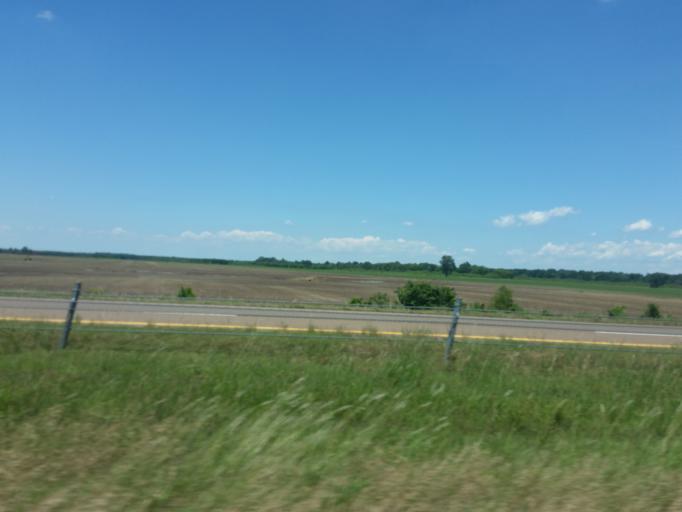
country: US
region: Missouri
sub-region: Pemiscot County
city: Caruthersville
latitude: 36.0868
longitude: -89.5573
